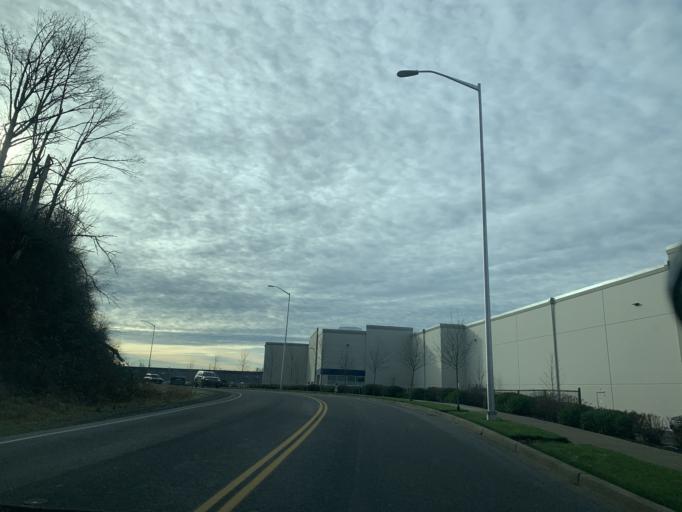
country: US
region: Washington
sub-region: Pierce County
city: Milton
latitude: 47.2326
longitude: -122.3239
